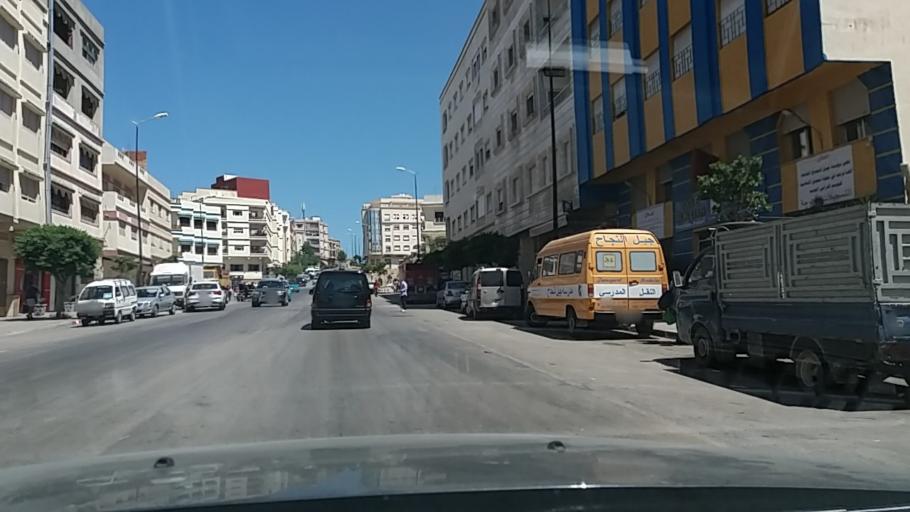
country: MA
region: Tanger-Tetouan
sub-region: Tanger-Assilah
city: Tangier
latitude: 35.7642
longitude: -5.7945
